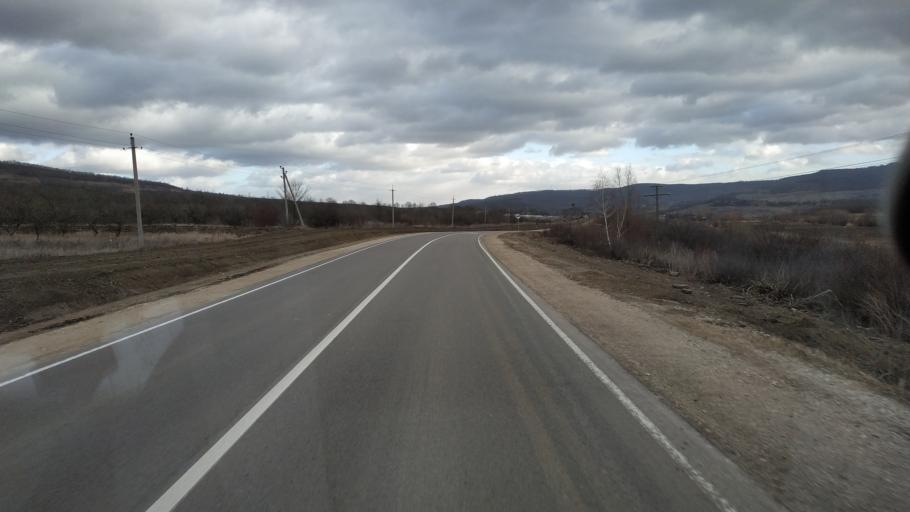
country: MD
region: Calarasi
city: Calarasi
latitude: 47.2652
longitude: 28.2320
